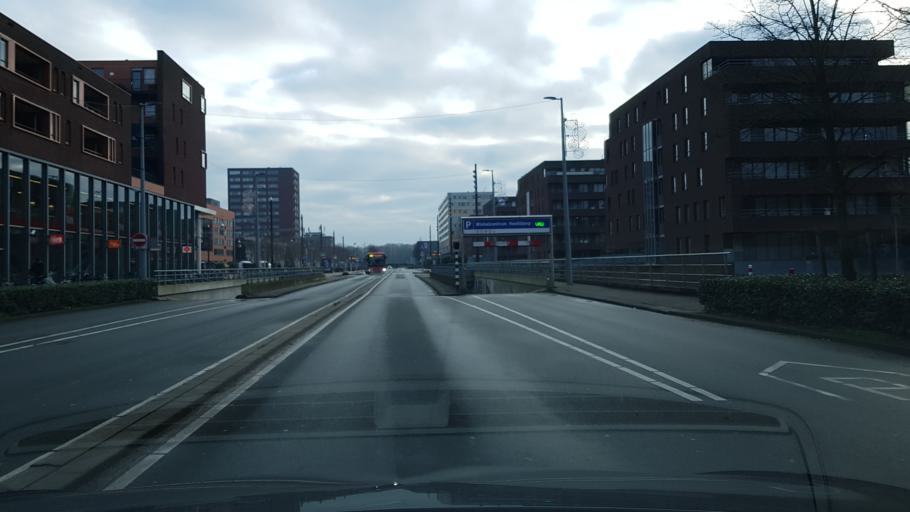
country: NL
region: North Holland
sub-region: Gemeente Haarlemmermeer
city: Hoofddorp
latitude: 52.3027
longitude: 4.6901
